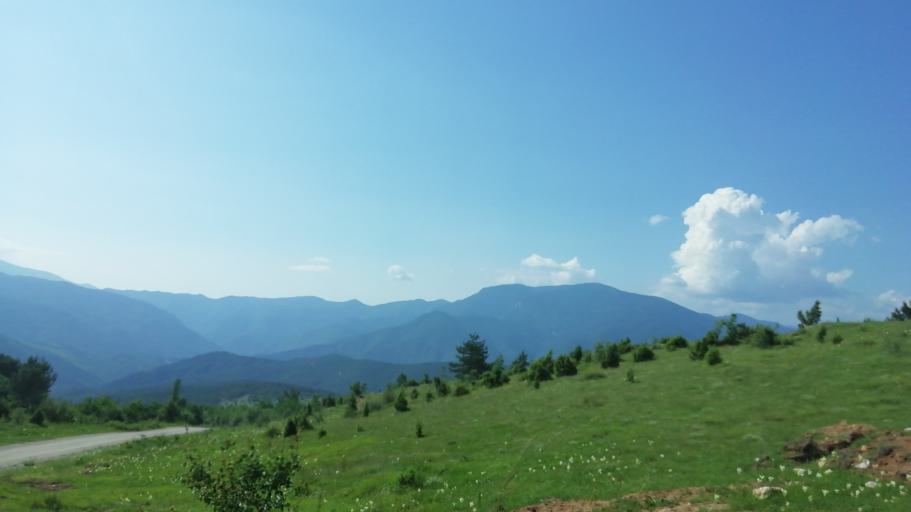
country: TR
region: Karabuk
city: Karabuk
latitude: 41.1243
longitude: 32.5812
